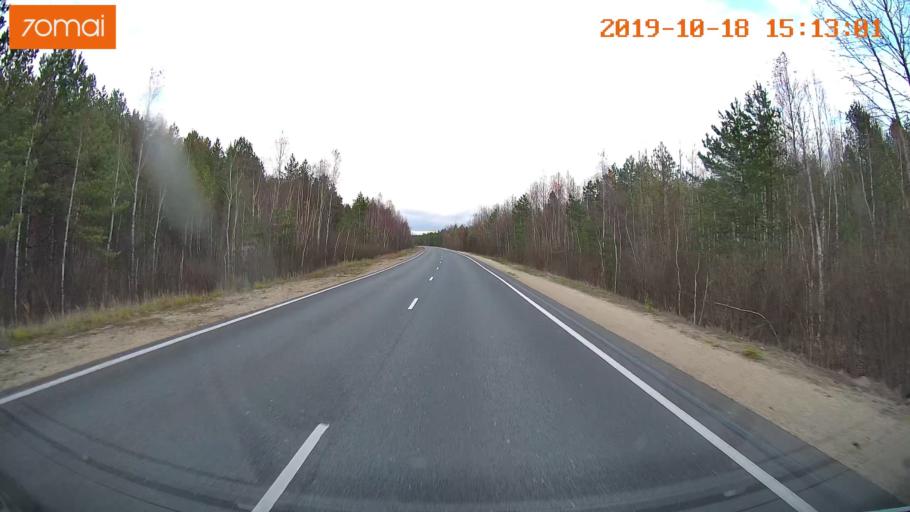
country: RU
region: Vladimir
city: Gus'-Khrustal'nyy
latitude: 55.5813
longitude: 40.7110
